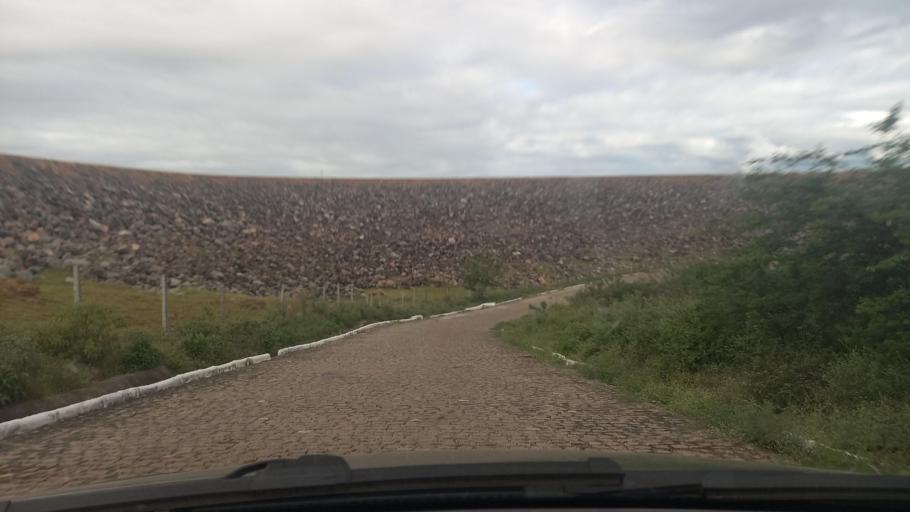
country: BR
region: Sergipe
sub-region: Caninde De Sao Francisco
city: Caninde de Sao Francisco
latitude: -9.6203
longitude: -37.8037
